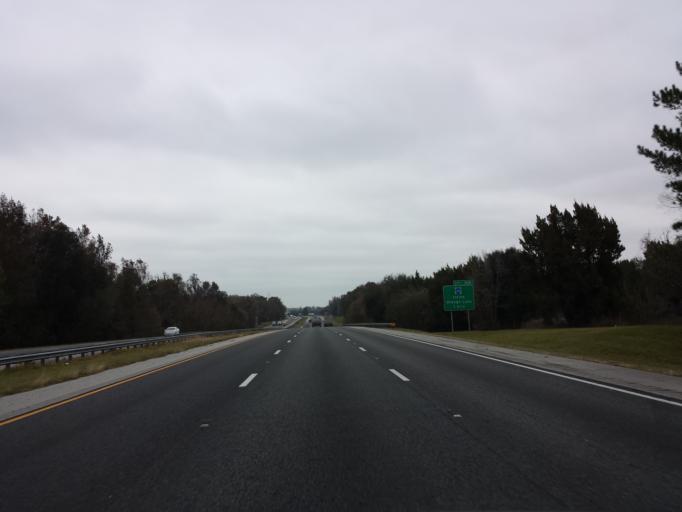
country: US
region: Florida
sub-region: Marion County
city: Citra
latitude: 29.3907
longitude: -82.2376
